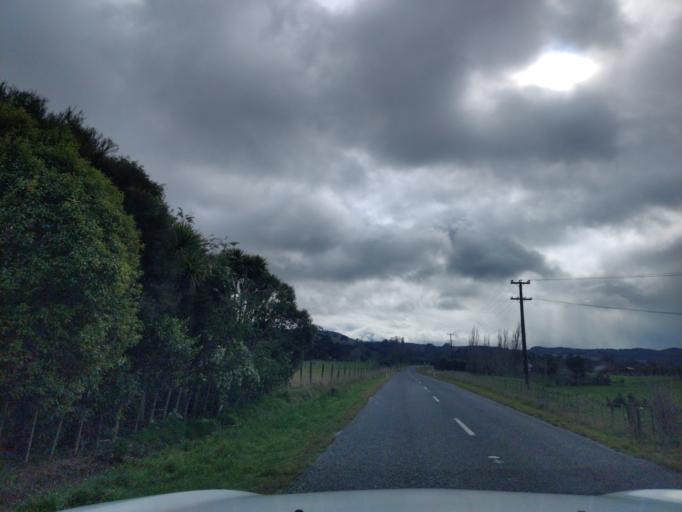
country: NZ
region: Manawatu-Wanganui
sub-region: Palmerston North City
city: Palmerston North
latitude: -40.1906
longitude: 175.7816
